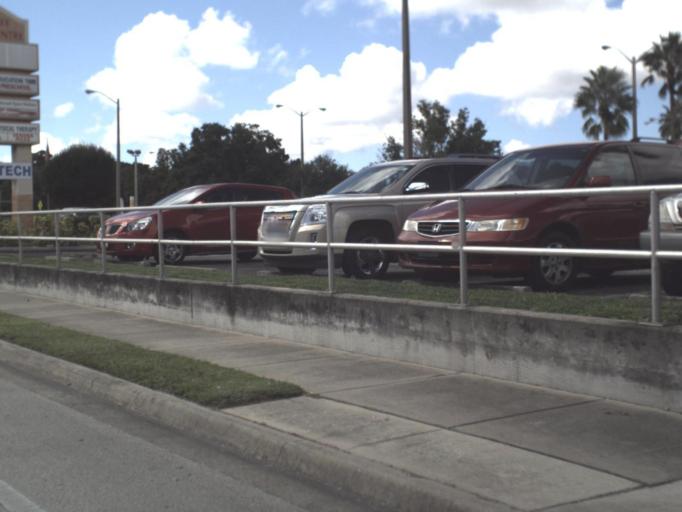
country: US
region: Florida
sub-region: Manatee County
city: Samoset
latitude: 27.4474
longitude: -82.5200
